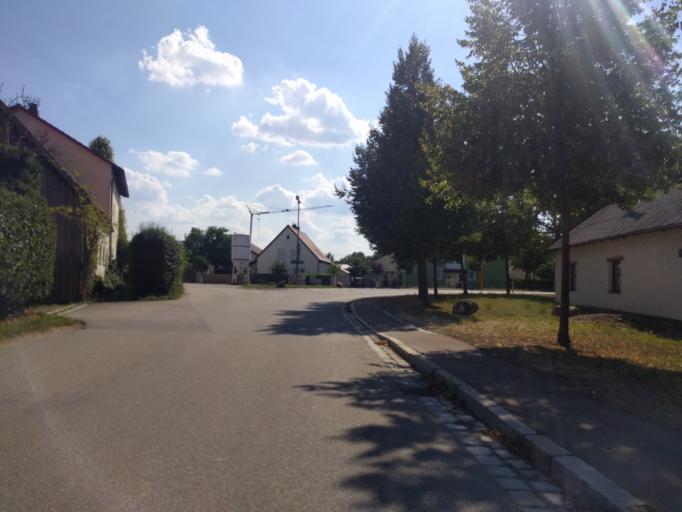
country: DE
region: Bavaria
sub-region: Upper Palatinate
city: Tegernheim
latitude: 49.0033
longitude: 12.1683
